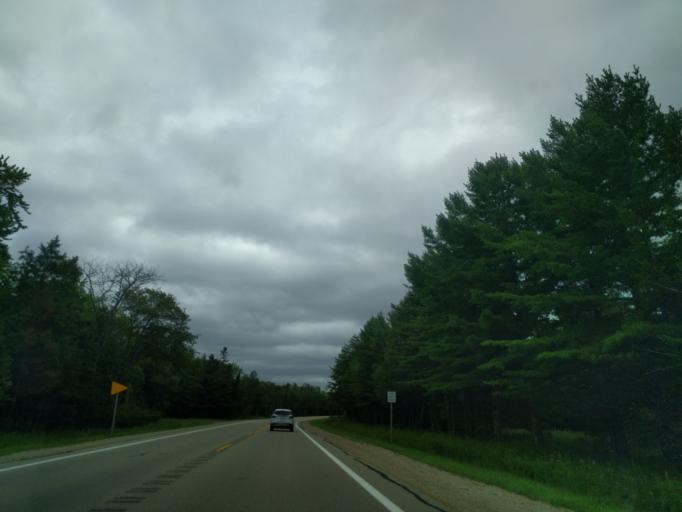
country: US
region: Michigan
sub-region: Delta County
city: Escanaba
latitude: 45.4769
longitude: -87.3088
